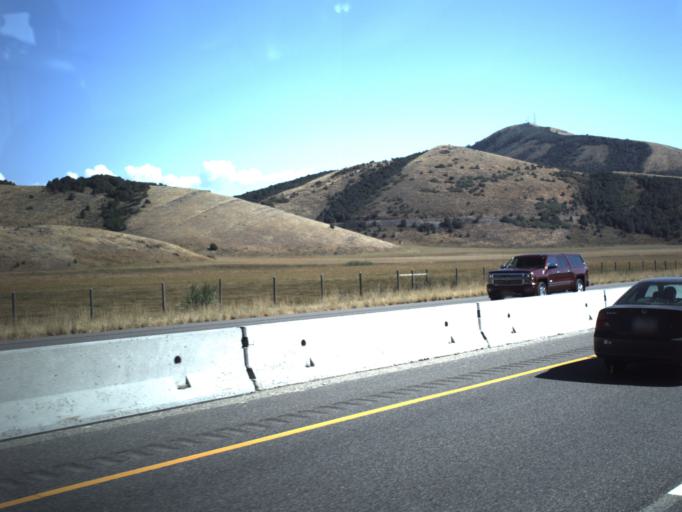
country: US
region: Utah
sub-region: Box Elder County
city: Brigham City
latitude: 41.5692
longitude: -111.9675
